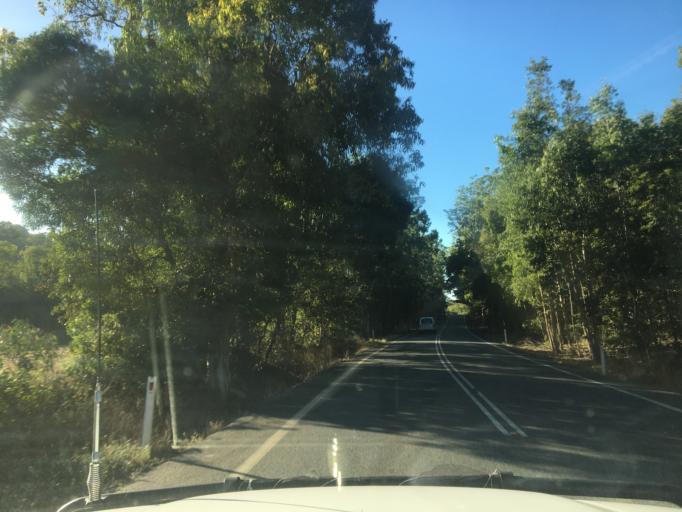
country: AU
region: Queensland
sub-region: Cairns
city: Port Douglas
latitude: -16.5896
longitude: 145.5136
